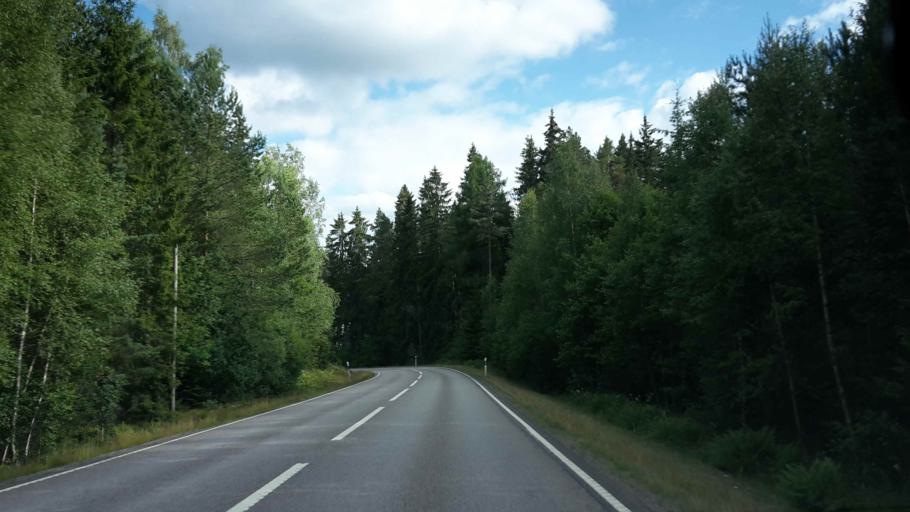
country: SE
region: OEstergoetland
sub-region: Motala Kommun
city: Borensberg
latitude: 58.8039
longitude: 15.4211
